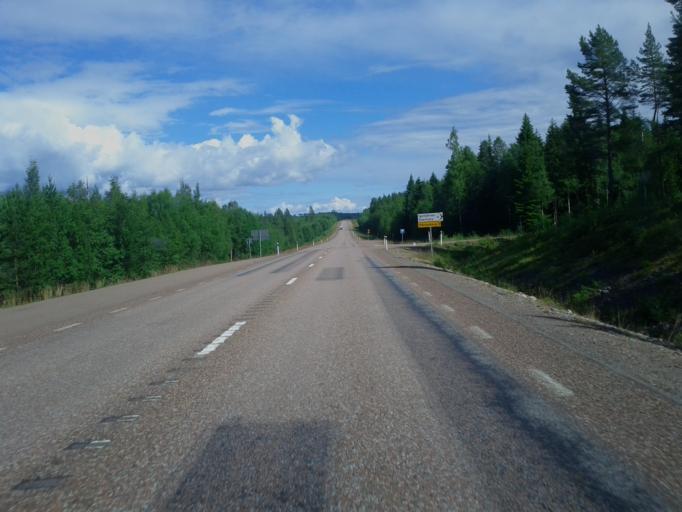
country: SE
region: Dalarna
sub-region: Rattviks Kommun
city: Raettvik
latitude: 60.8423
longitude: 15.1958
